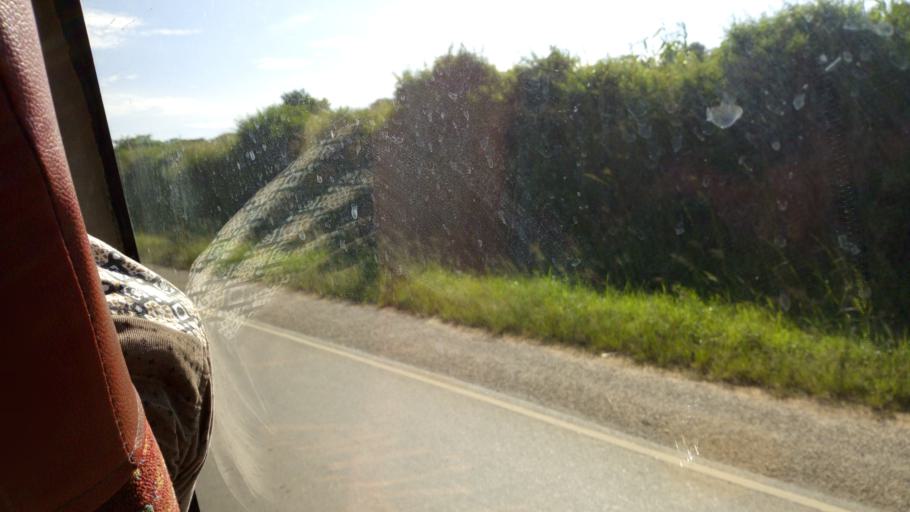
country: UG
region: Western Region
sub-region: Mbarara District
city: Mbarara
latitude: -0.4981
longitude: 30.8526
